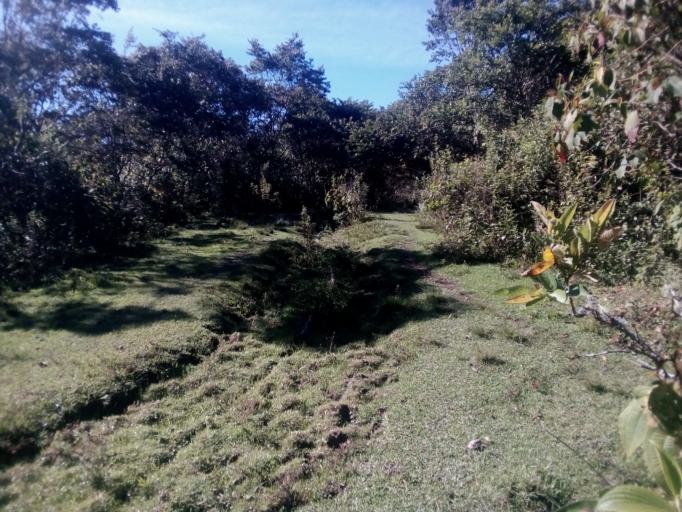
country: CO
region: Santander
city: Guepsa
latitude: 5.9906
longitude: -73.5534
